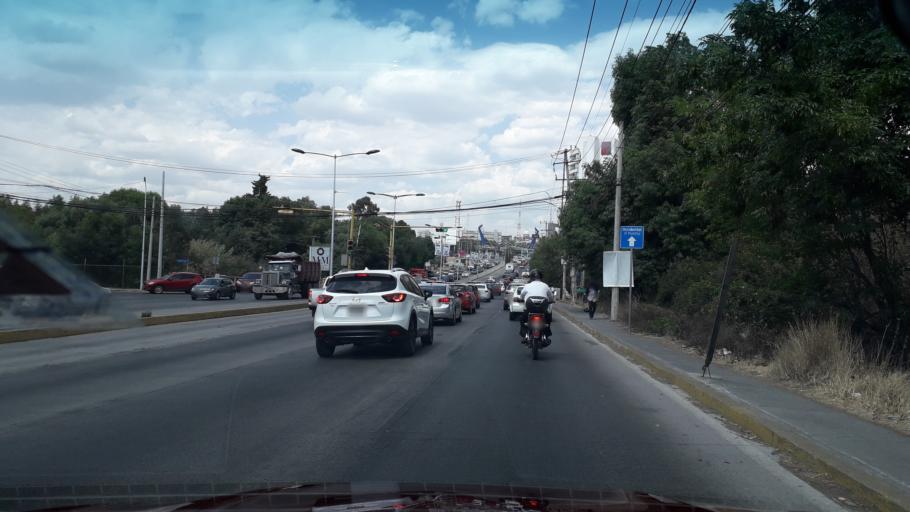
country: MX
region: Puebla
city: Puebla
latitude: 19.0413
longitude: -98.2380
